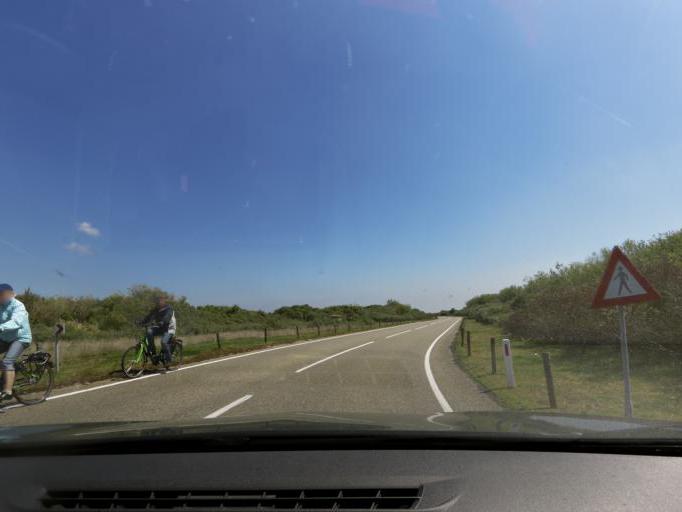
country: NL
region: Zeeland
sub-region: Schouwen-Duiveland
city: Burgh
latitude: 51.6342
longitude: 3.7068
